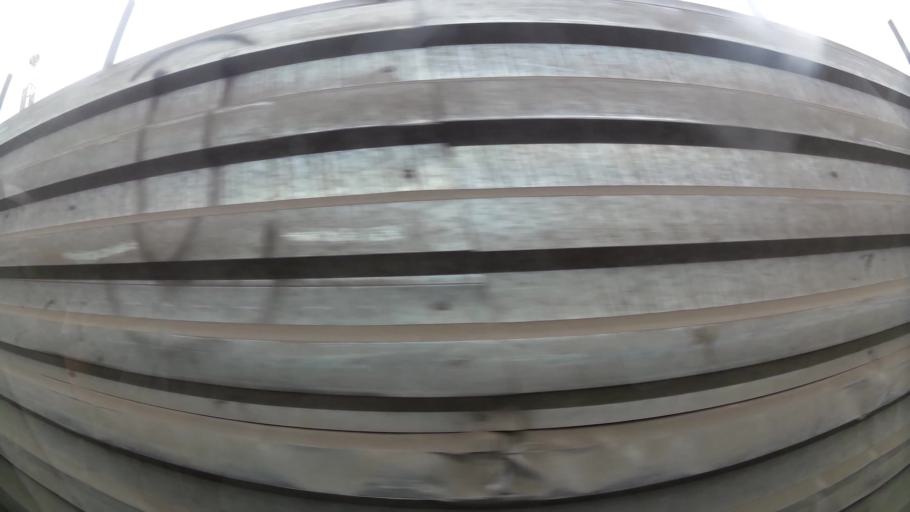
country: PE
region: Lima
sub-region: Lima
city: Vitarte
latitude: -12.0446
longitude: -76.9395
